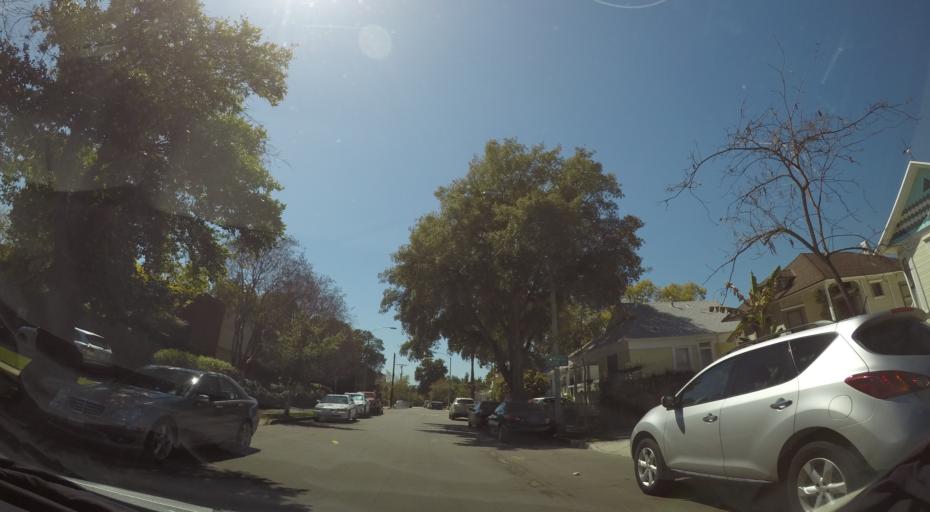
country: US
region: California
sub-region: Los Angeles County
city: Pasadena
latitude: 34.1538
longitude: -118.1524
